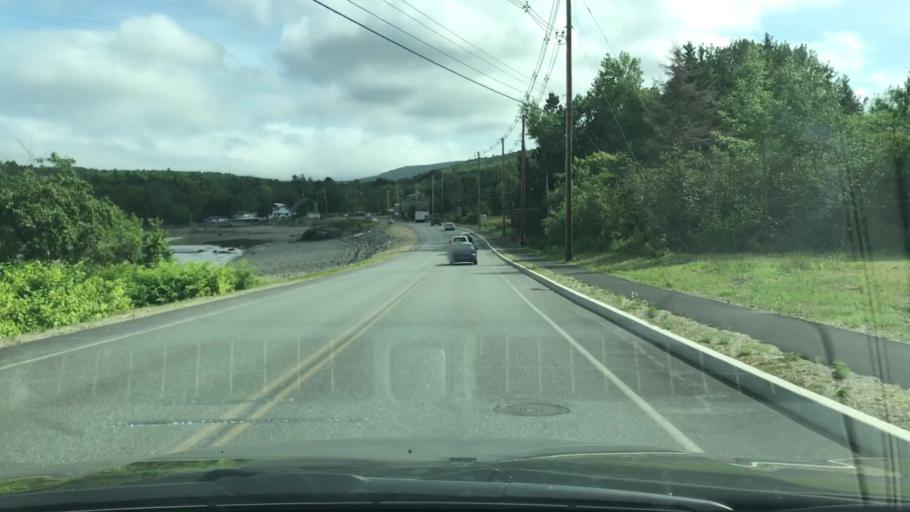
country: US
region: Maine
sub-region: Hancock County
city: Bar Harbor
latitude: 44.4183
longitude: -68.2504
